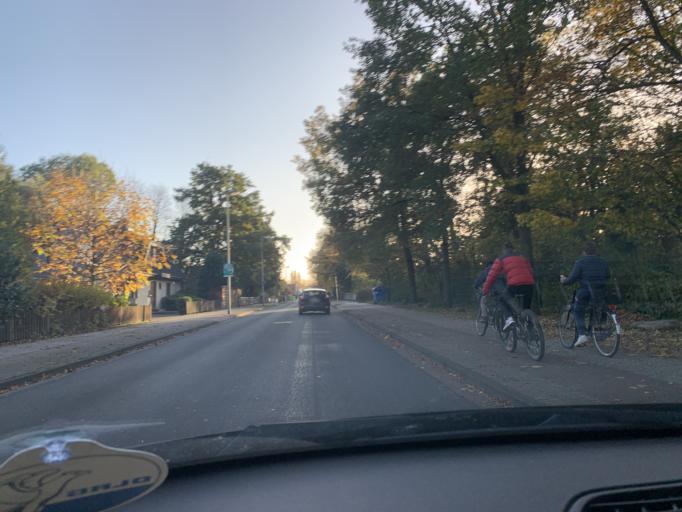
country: DE
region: Lower Saxony
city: Oldenburg
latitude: 53.1459
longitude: 8.1790
